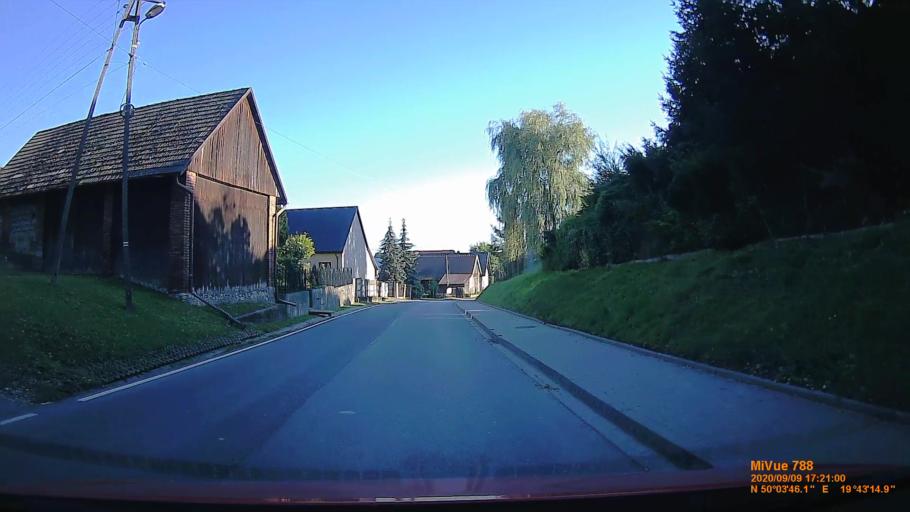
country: PL
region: Lesser Poland Voivodeship
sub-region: Powiat krakowski
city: Mnikow
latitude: 50.0627
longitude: 19.7208
